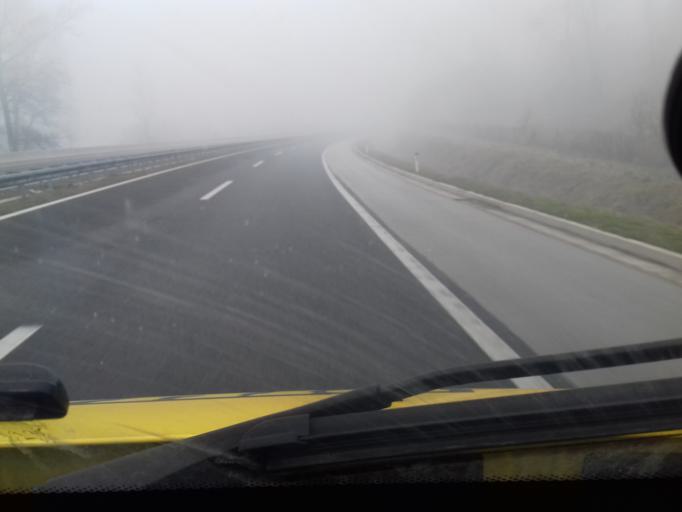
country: BA
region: Federation of Bosnia and Herzegovina
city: Kakanj
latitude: 44.1062
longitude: 18.1111
